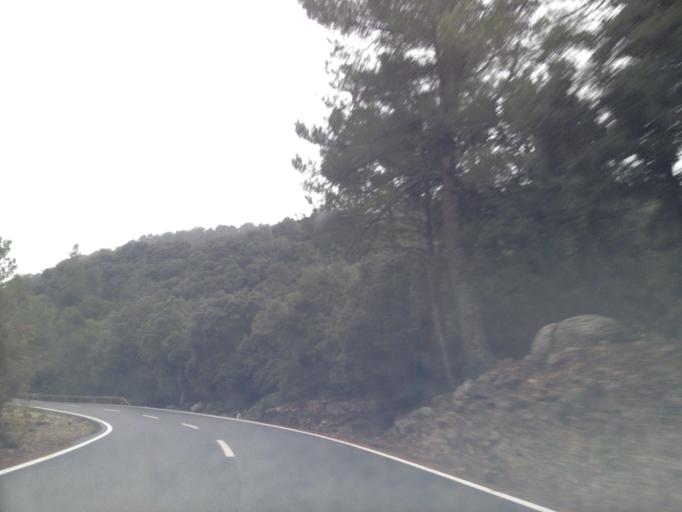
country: ES
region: Balearic Islands
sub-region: Illes Balears
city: Fornalutx
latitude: 39.7958
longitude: 2.7712
